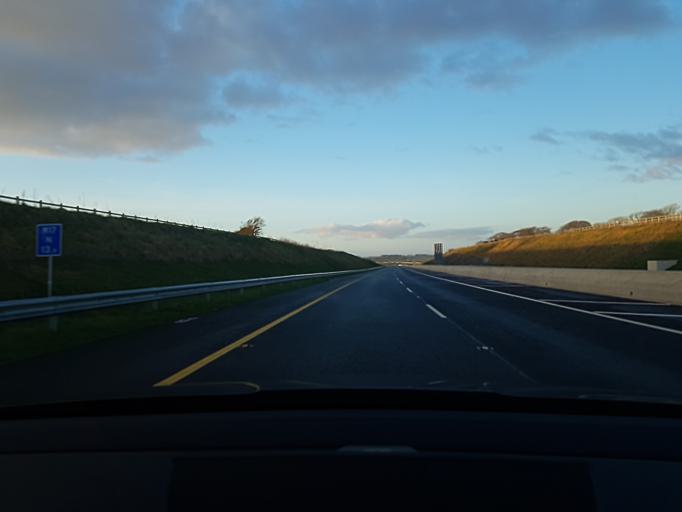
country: IE
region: Connaught
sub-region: County Galway
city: Tuam
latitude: 53.4088
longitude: -8.8258
